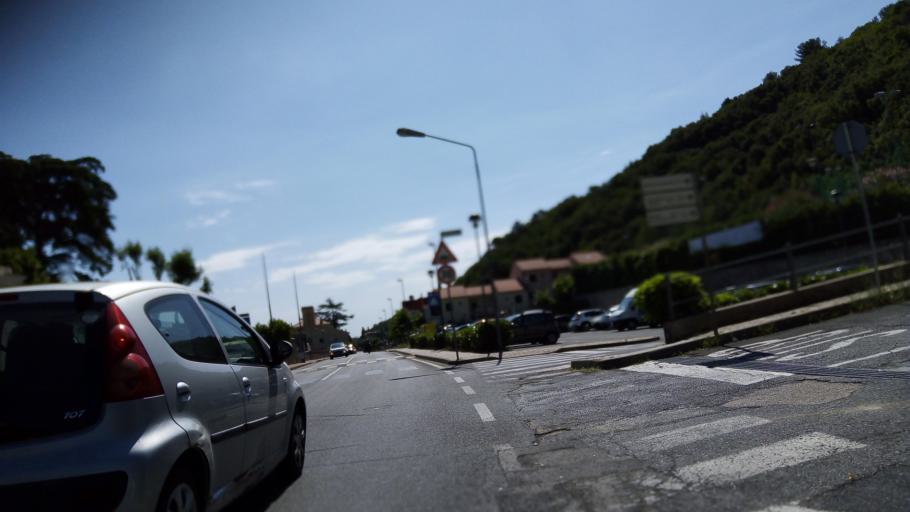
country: IT
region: Liguria
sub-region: Provincia di Savona
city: Toirano
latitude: 44.1251
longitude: 8.2083
